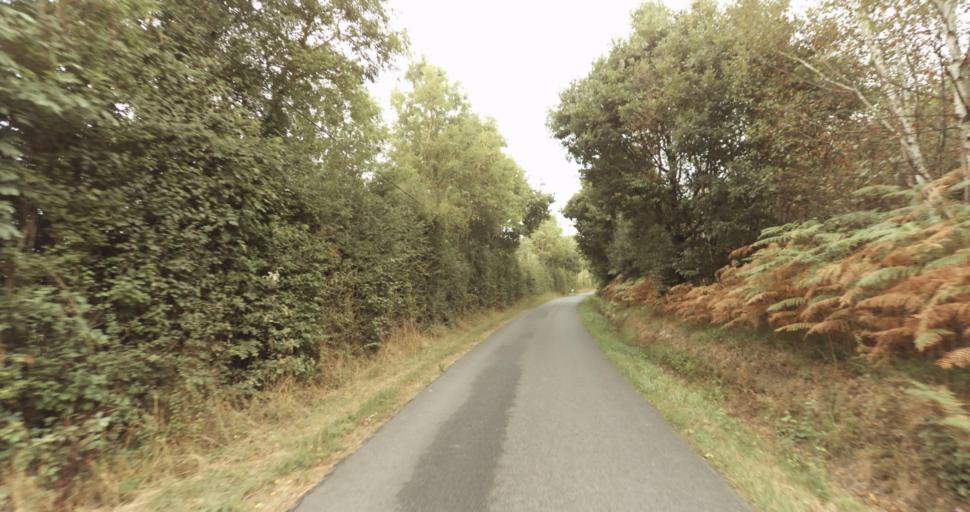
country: FR
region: Lower Normandy
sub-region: Departement de l'Orne
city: Gace
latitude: 48.8351
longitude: 0.3344
